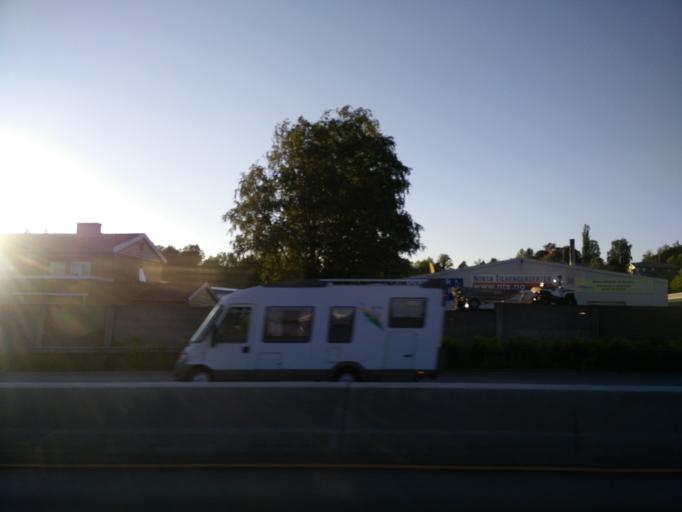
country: NO
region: Akershus
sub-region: Baerum
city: Sandvika
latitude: 59.8969
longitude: 10.5646
